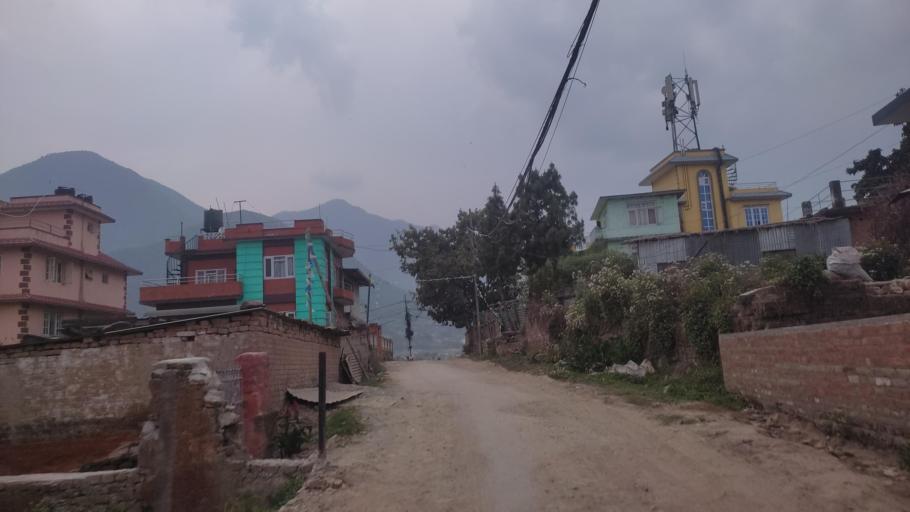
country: NP
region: Central Region
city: Kirtipur
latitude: 27.6616
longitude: 85.2786
